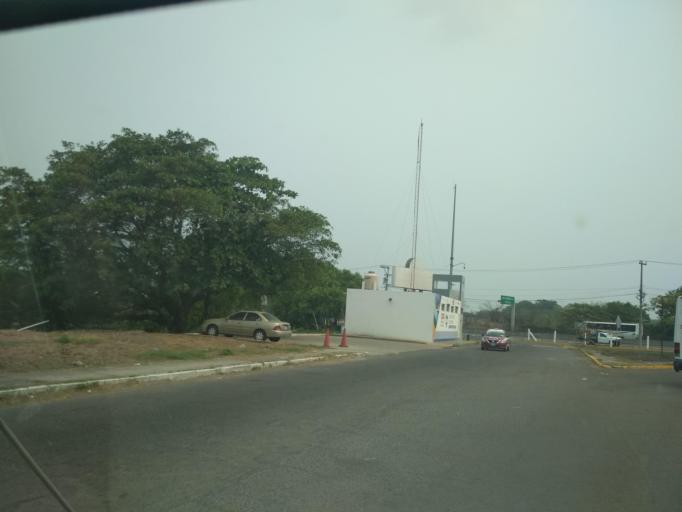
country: MX
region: Veracruz
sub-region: Veracruz
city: Fraccionamiento Geovillas los Pinos
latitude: 19.2189
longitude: -96.2240
